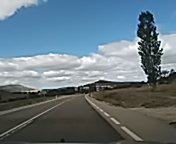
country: ES
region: Castille and Leon
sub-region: Provincia de Burgos
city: Hontoria del Pinar
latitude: 41.8465
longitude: -3.1465
